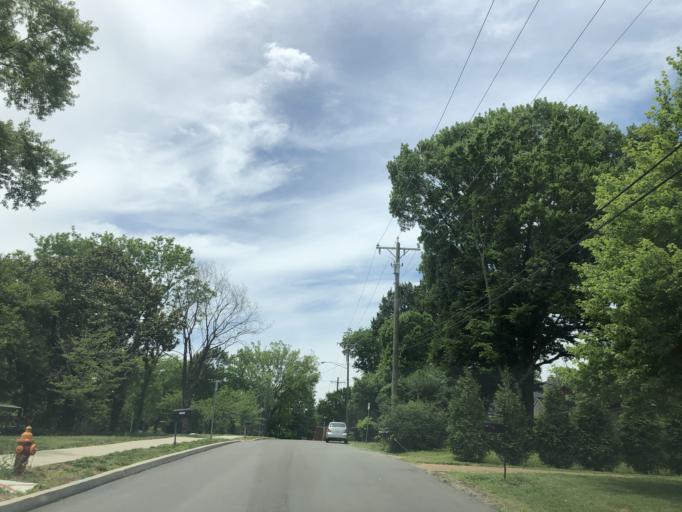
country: US
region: Tennessee
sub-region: Davidson County
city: Oak Hill
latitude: 36.1088
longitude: -86.7990
